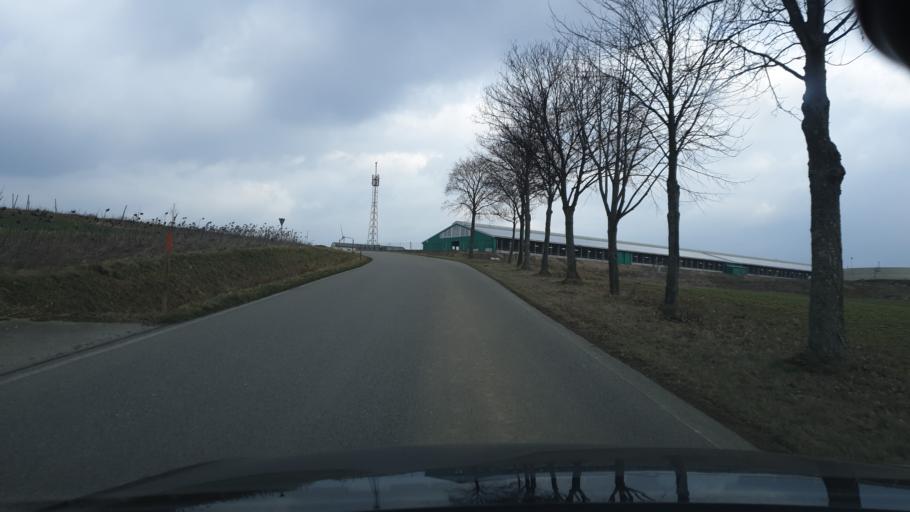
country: DE
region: Saxony
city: Erlau
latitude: 51.0000
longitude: 12.9153
